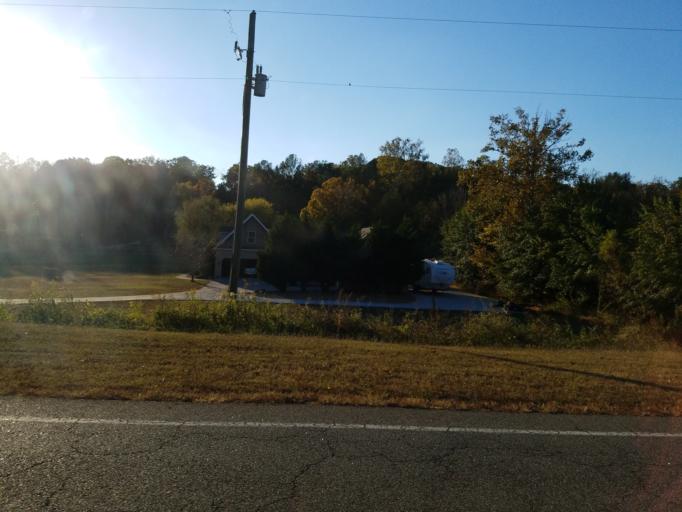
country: US
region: Georgia
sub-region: Bartow County
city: Adairsville
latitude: 34.3220
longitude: -84.9364
